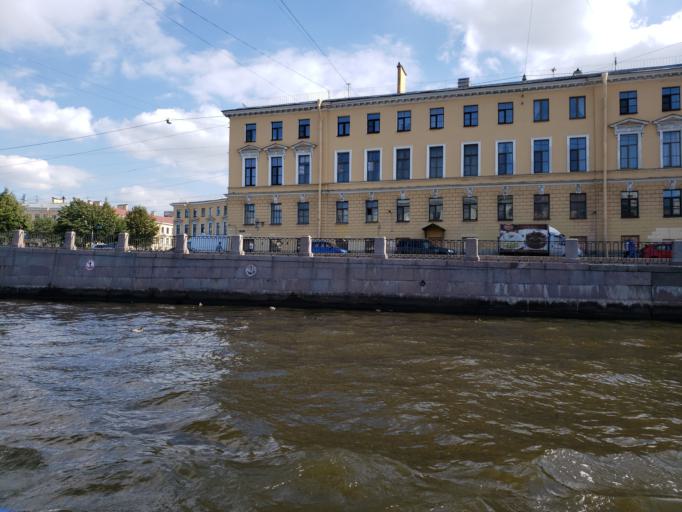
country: RU
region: St.-Petersburg
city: Saint Petersburg
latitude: 59.9247
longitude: 30.3258
